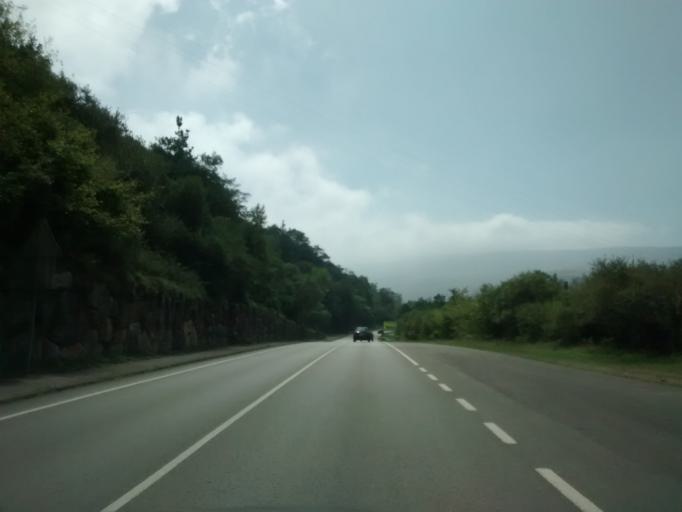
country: ES
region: Cantabria
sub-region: Provincia de Cantabria
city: Ruente
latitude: 43.2747
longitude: -4.2457
